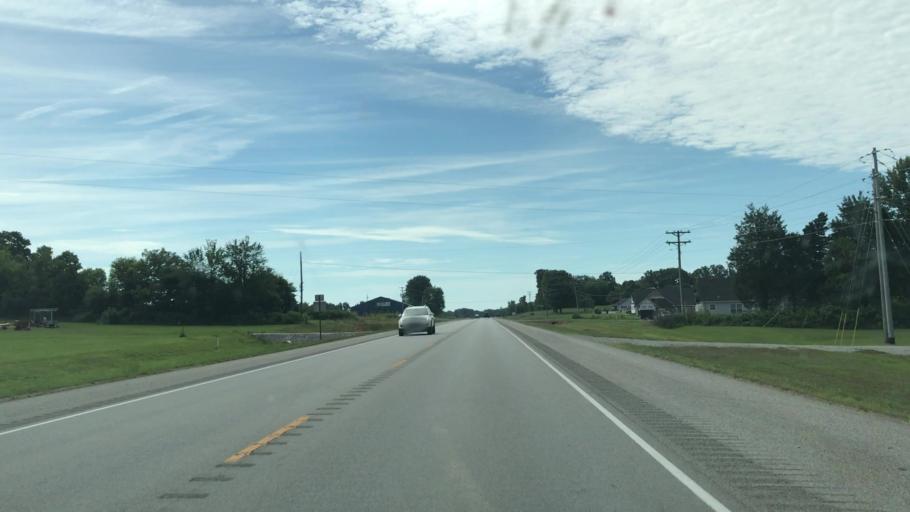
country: US
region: Kentucky
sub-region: Edmonson County
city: Brownsville
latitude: 37.1716
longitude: -86.2334
